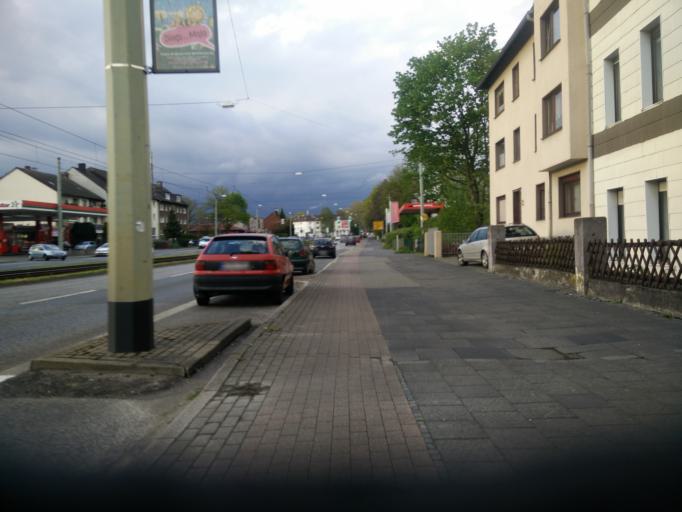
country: DE
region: North Rhine-Westphalia
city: Bochum-Hordel
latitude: 51.5007
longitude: 7.1890
